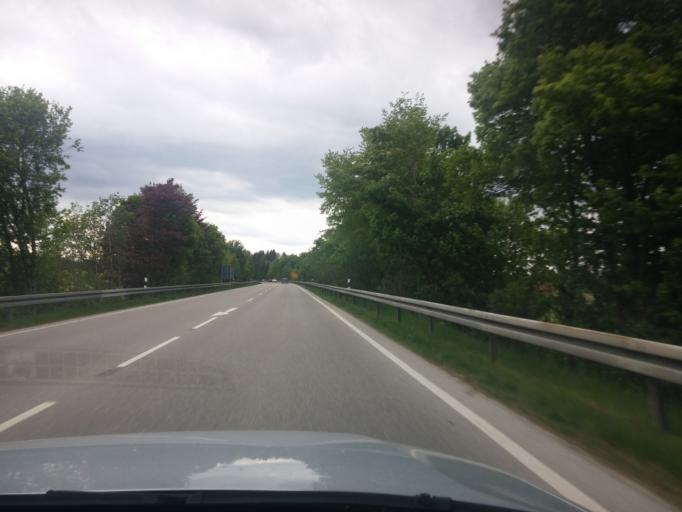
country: DE
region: Bavaria
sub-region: Upper Bavaria
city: Sachsenkam
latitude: 47.8007
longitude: 11.6450
